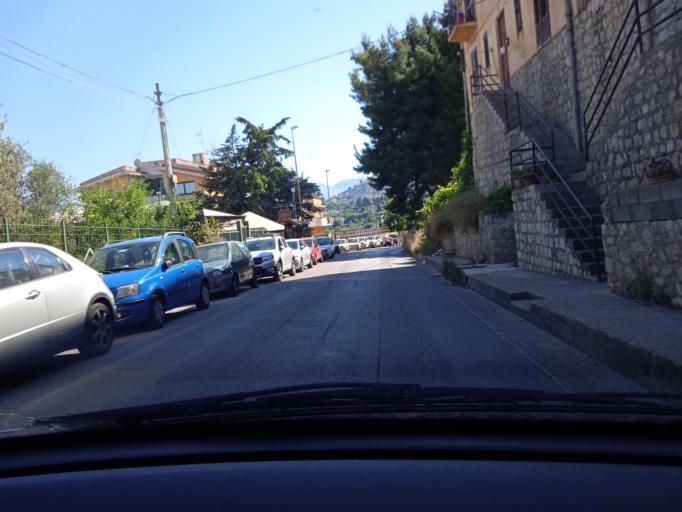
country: IT
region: Sicily
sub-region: Palermo
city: Monreale
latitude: 38.0779
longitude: 13.2818
